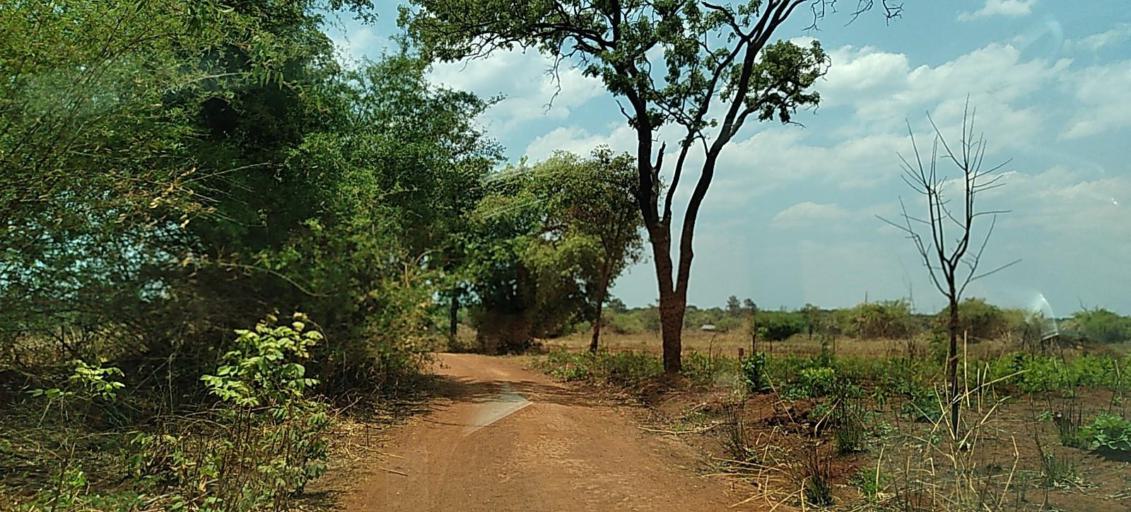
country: ZM
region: Copperbelt
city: Chingola
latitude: -12.5436
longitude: 27.6320
